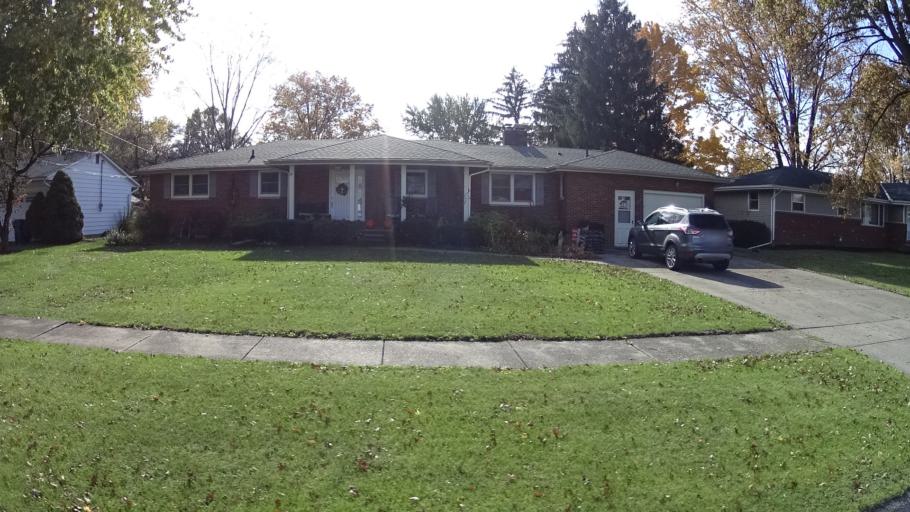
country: US
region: Ohio
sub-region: Lorain County
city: Lorain
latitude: 41.4436
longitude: -82.2177
